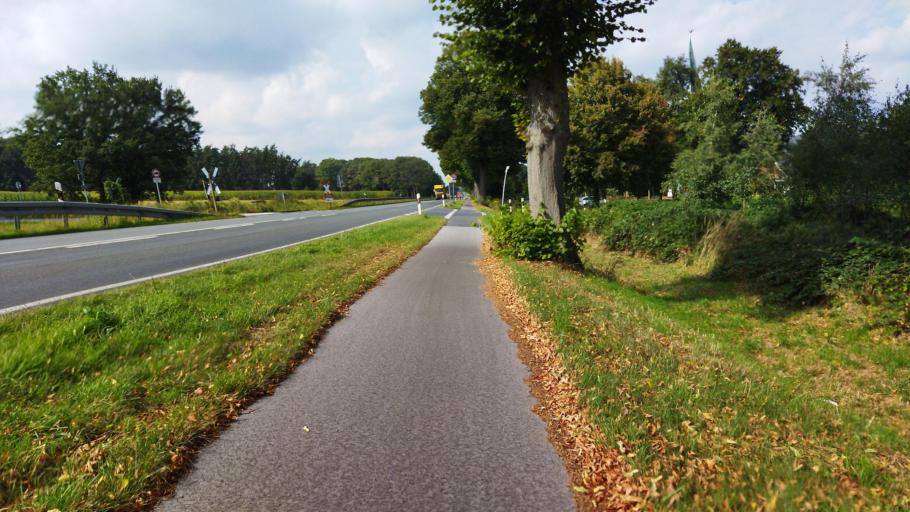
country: DE
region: North Rhine-Westphalia
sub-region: Regierungsbezirk Munster
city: Everswinkel
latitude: 51.9664
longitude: 7.8606
